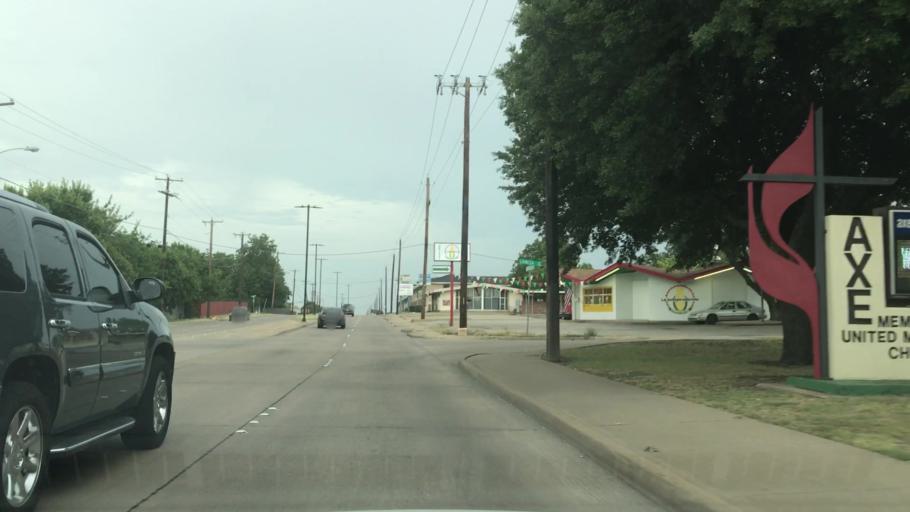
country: US
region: Texas
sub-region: Dallas County
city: Garland
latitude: 32.8787
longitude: -96.6528
